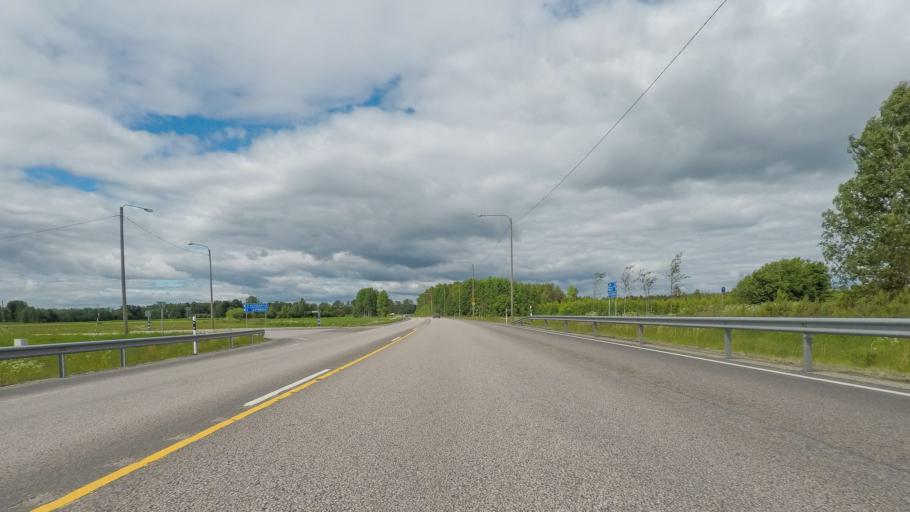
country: FI
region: Paijanne Tavastia
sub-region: Lahti
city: Hartola
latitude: 61.6059
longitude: 26.0090
